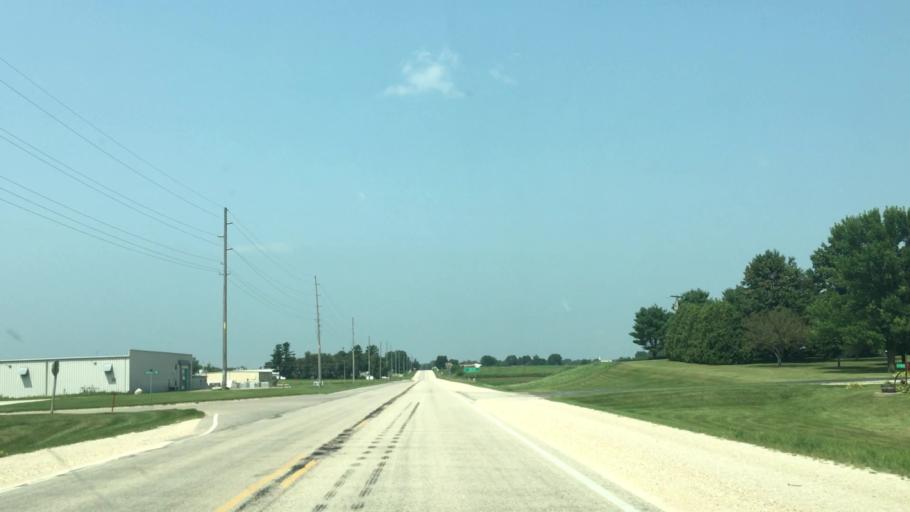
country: US
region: Iowa
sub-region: Fayette County
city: West Union
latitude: 42.9409
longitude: -91.8142
